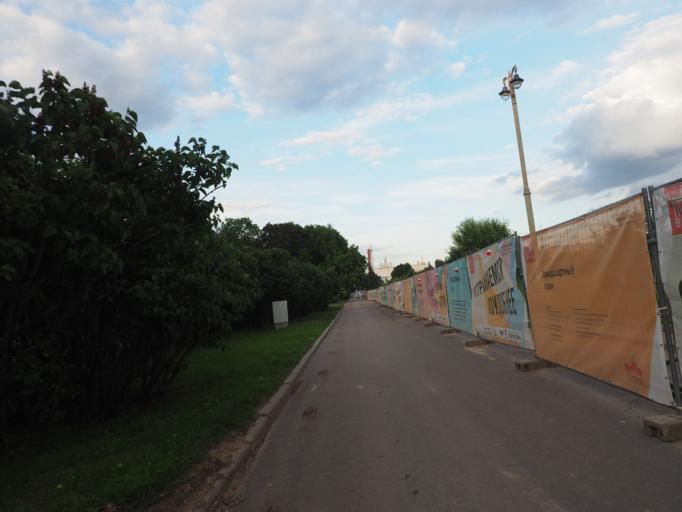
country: RU
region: Moscow
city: Ostankinskiy
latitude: 55.8346
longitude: 37.6156
